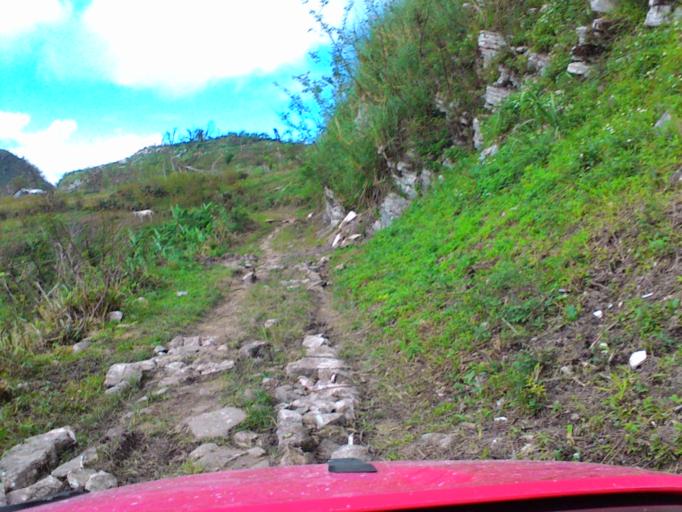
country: HT
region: Grandans
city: Moron
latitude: 18.4624
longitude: -74.1126
